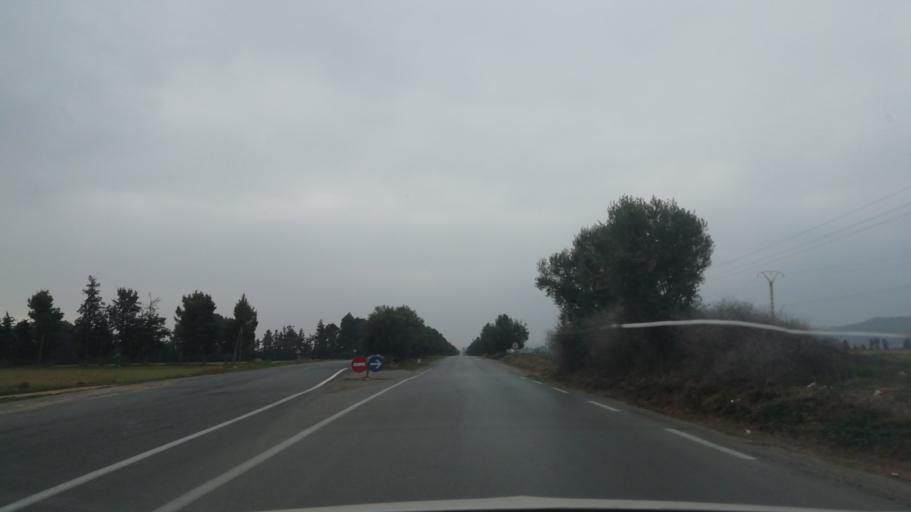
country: DZ
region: Sidi Bel Abbes
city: Sfizef
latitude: 35.2271
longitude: -0.2698
